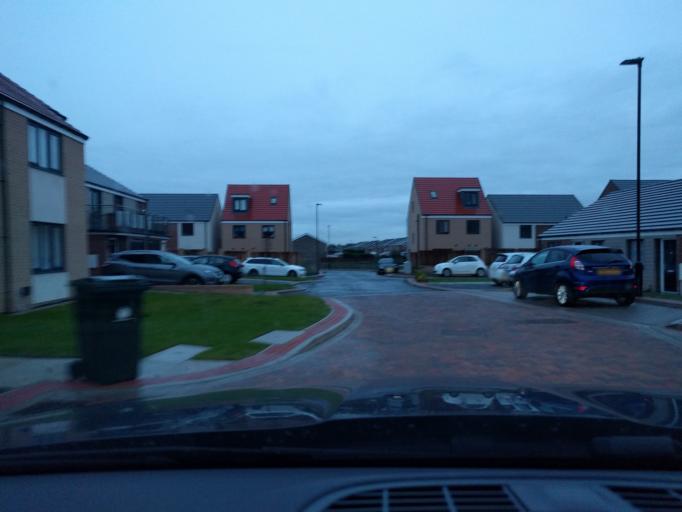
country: GB
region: England
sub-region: Borough of North Tyneside
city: Wallsend
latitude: 55.0107
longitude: -1.5461
